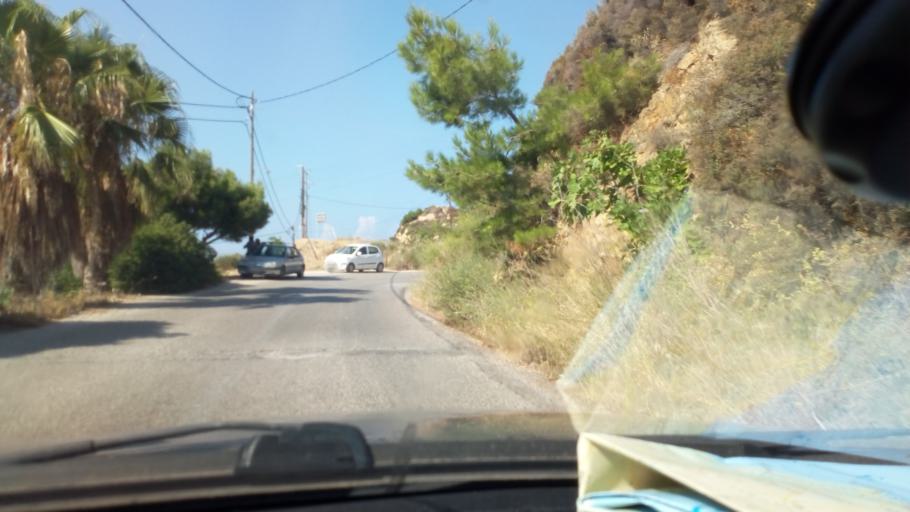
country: GR
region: North Aegean
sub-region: Nomos Samou
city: Agios Kirykos
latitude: 37.6286
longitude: 26.0905
